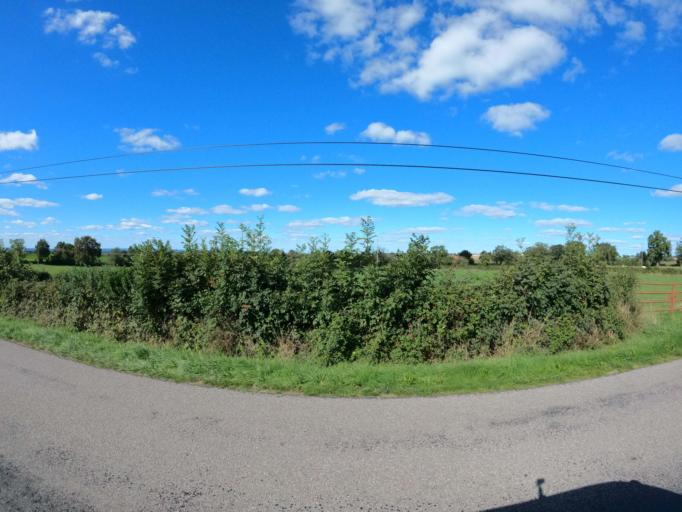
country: FR
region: Auvergne
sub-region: Departement de l'Allier
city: Buxieres-les-Mines
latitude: 46.4028
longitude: 2.9372
